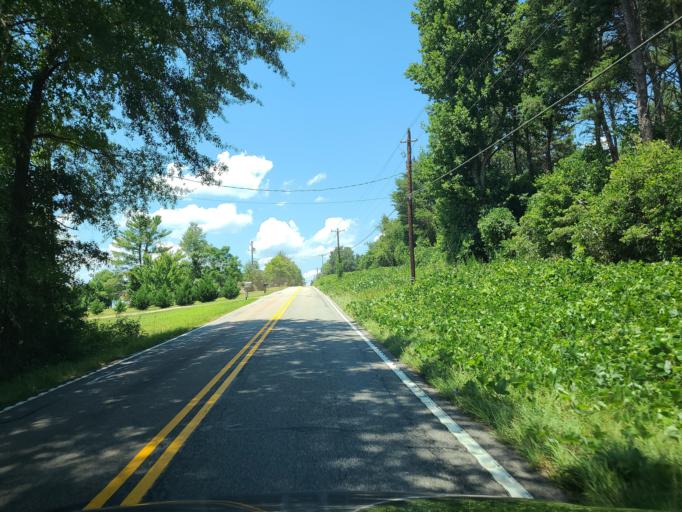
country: US
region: South Carolina
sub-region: Spartanburg County
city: Duncan
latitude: 34.9804
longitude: -82.1770
